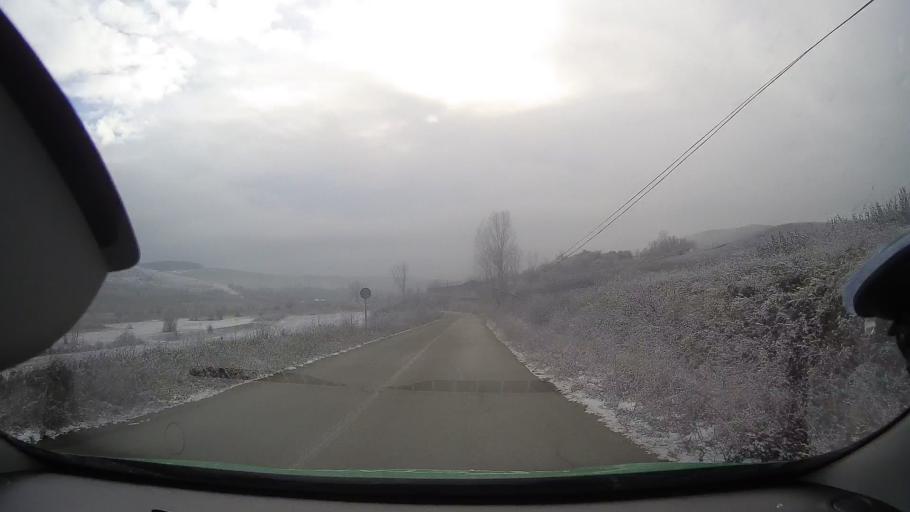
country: RO
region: Mures
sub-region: Comuna Chetani
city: Chetani
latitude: 46.4206
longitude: 24.0151
